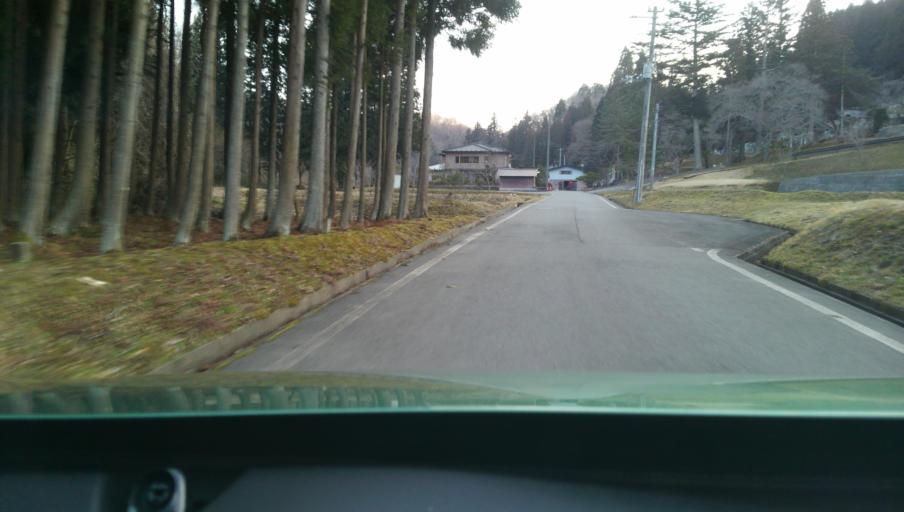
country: JP
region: Iwate
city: Ichinoseki
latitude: 38.9147
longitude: 141.0895
